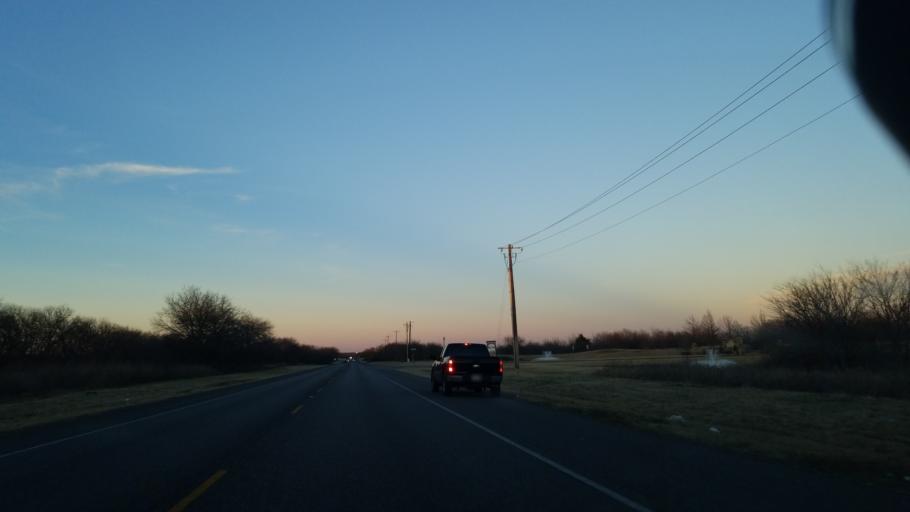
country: US
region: Texas
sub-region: Denton County
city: Argyle
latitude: 33.1426
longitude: -97.1724
